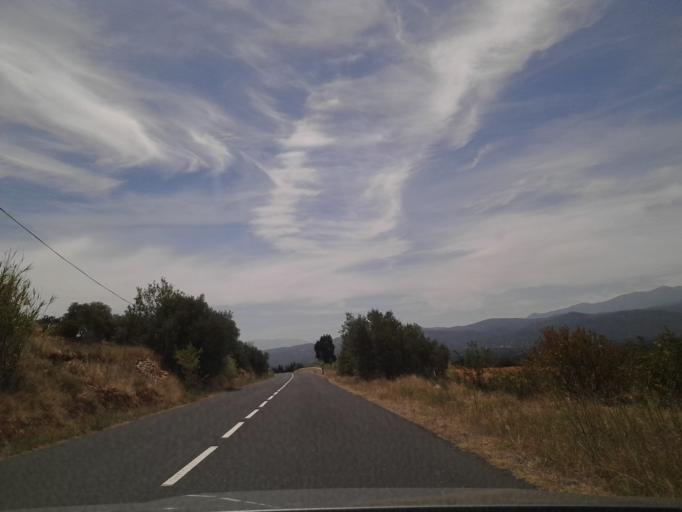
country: FR
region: Languedoc-Roussillon
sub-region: Departement des Pyrenees-Orientales
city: Millas
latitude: 42.7118
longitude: 2.6835
